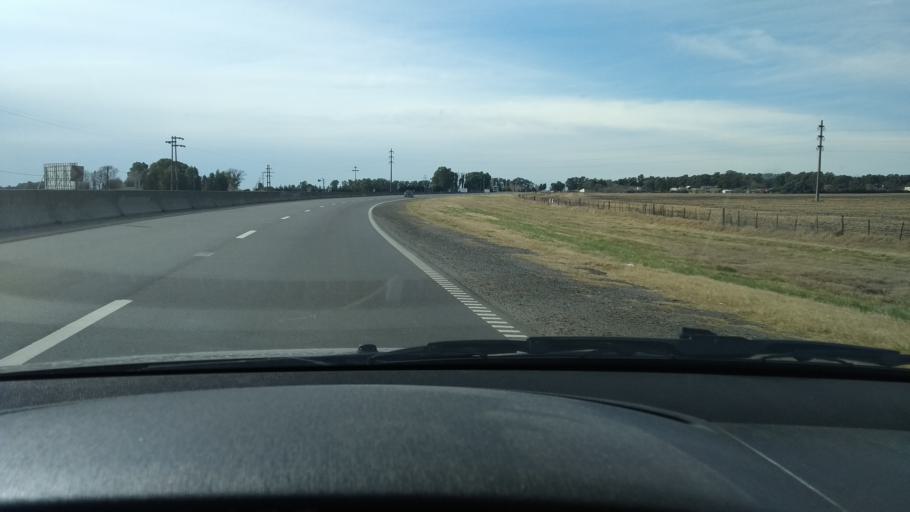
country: AR
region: Buenos Aires
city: Olavarria
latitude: -36.9041
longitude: -60.1889
